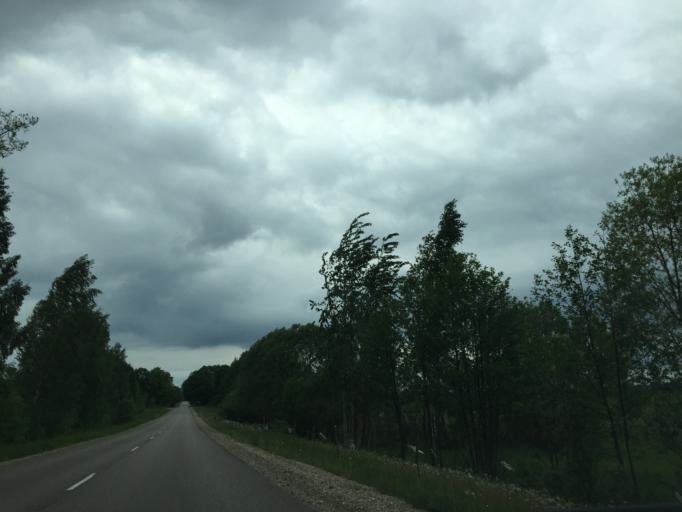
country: LV
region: Varkava
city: Vecvarkava
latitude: 56.0734
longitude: 26.7014
